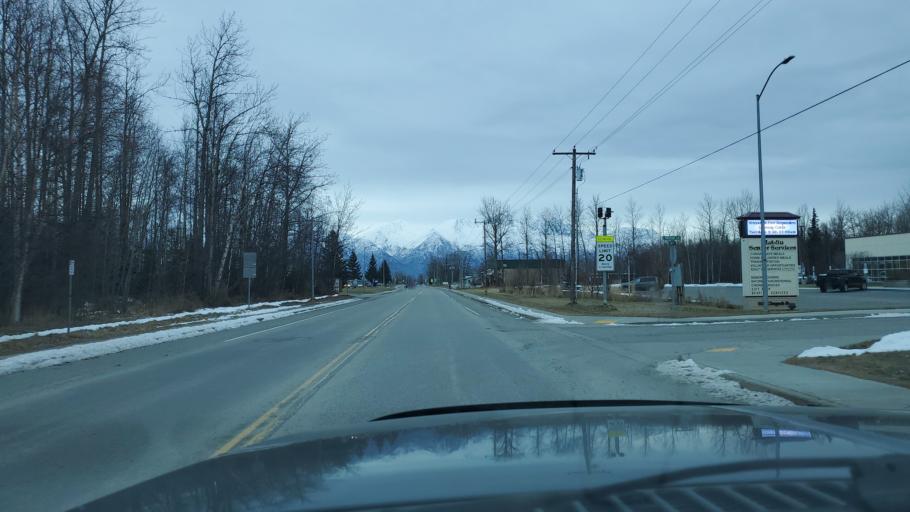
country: US
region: Alaska
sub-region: Matanuska-Susitna Borough
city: Palmer
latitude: 61.5952
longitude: -149.1108
